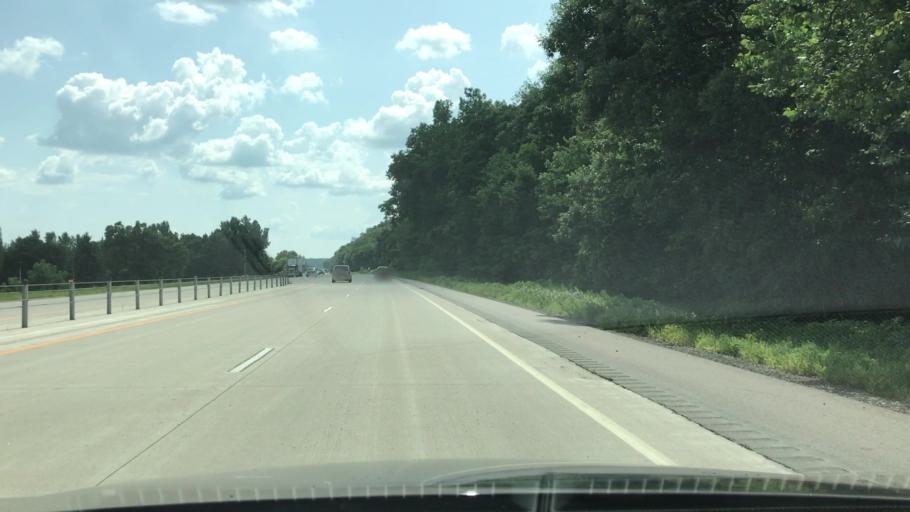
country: US
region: Minnesota
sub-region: Nicollet County
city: Saint Peter
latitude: 44.2929
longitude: -93.9966
